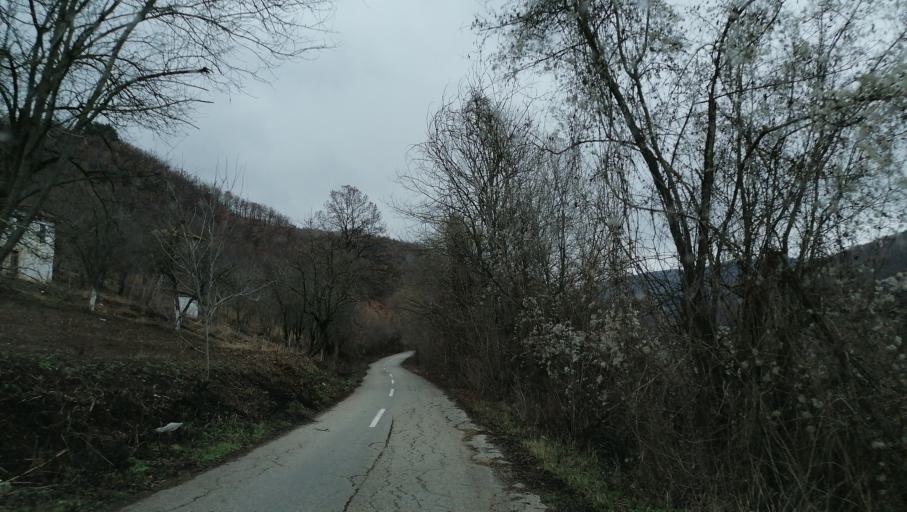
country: RS
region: Central Serbia
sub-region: Pirotski Okrug
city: Dimitrovgrad
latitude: 42.9612
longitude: 22.7824
